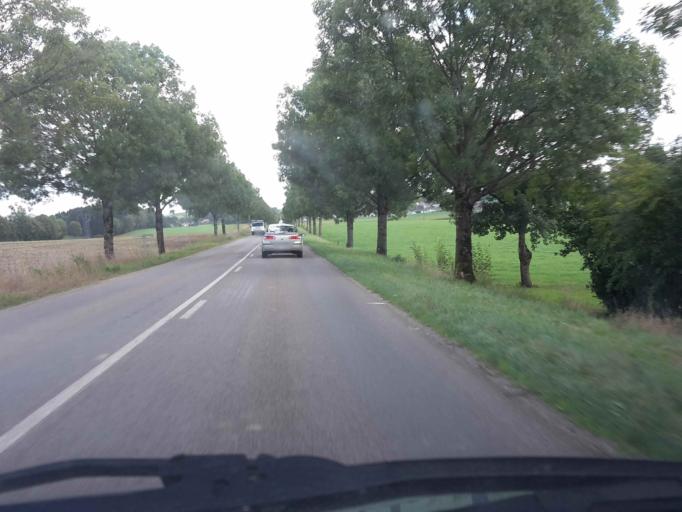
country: FR
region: Franche-Comte
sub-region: Departement du Doubs
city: Nancray
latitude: 47.2433
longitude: 6.1552
